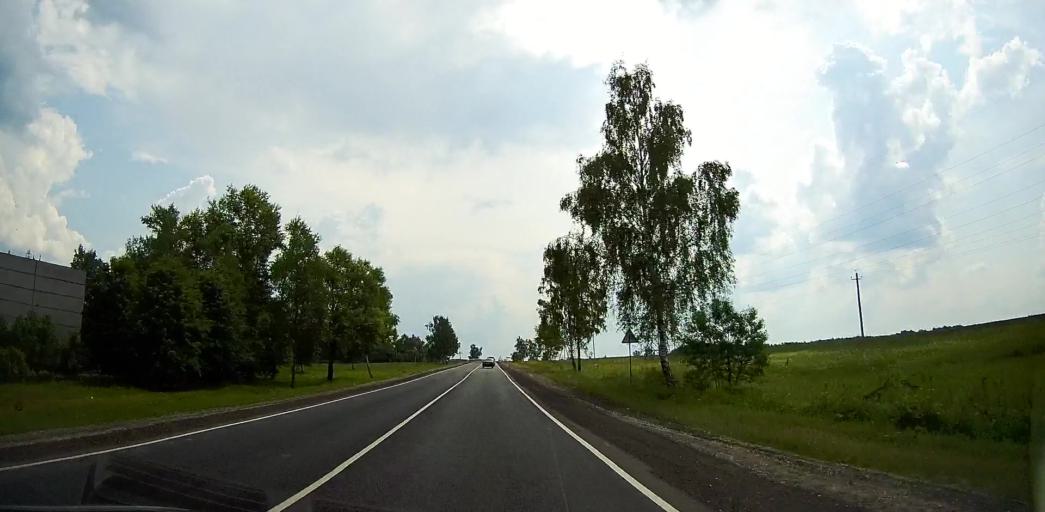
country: RU
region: Moskovskaya
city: Stupino
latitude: 54.9399
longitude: 38.1340
